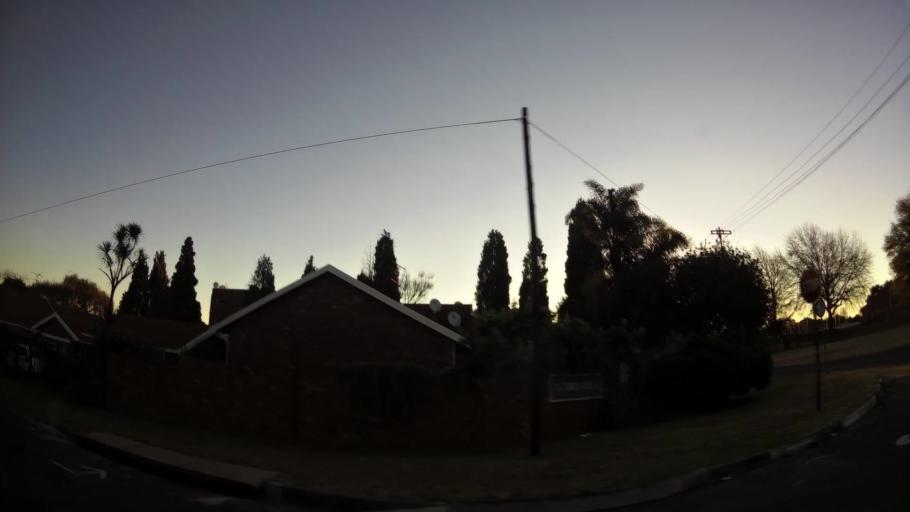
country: ZA
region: Gauteng
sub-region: City of Johannesburg Metropolitan Municipality
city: Roodepoort
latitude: -26.1548
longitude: 27.8879
